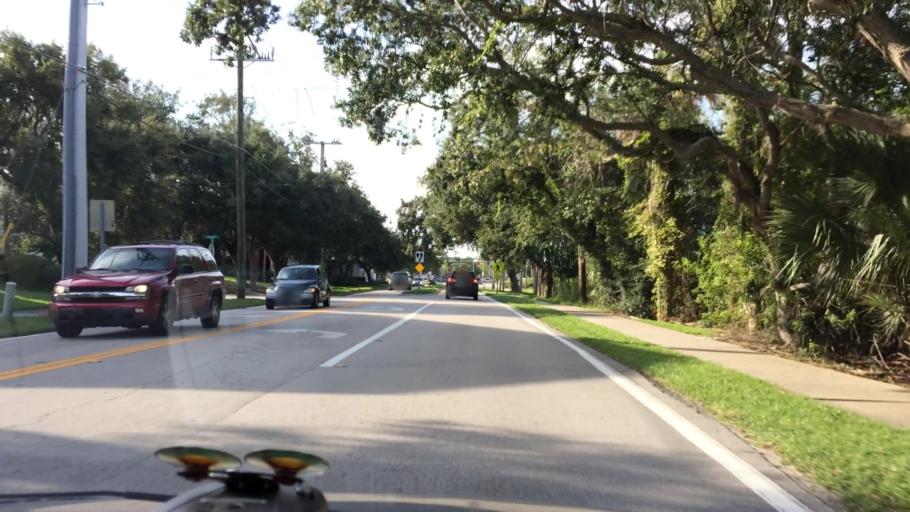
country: US
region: Florida
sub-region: Volusia County
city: Ormond Beach
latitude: 29.2836
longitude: -81.0546
